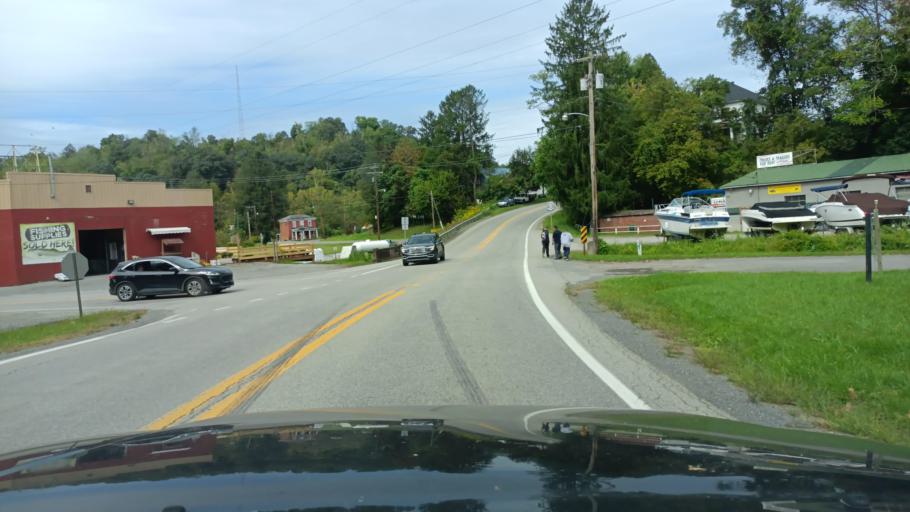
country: US
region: West Virginia
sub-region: Taylor County
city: Grafton
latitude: 39.3472
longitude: -80.0377
